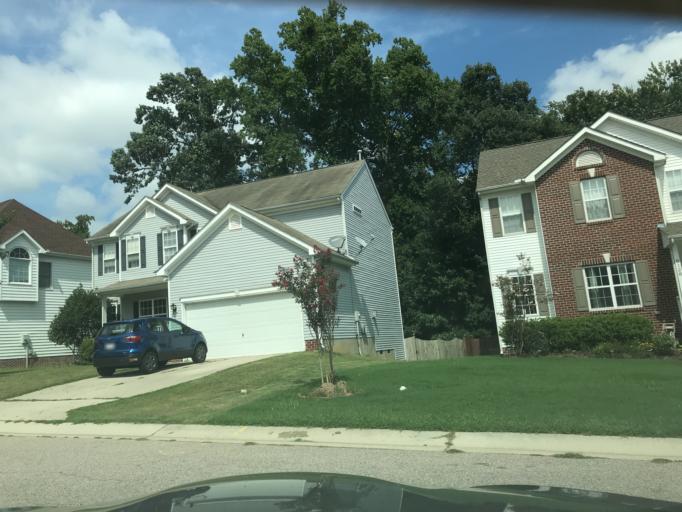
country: US
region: North Carolina
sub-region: Wake County
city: Rolesville
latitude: 35.8893
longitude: -78.5444
